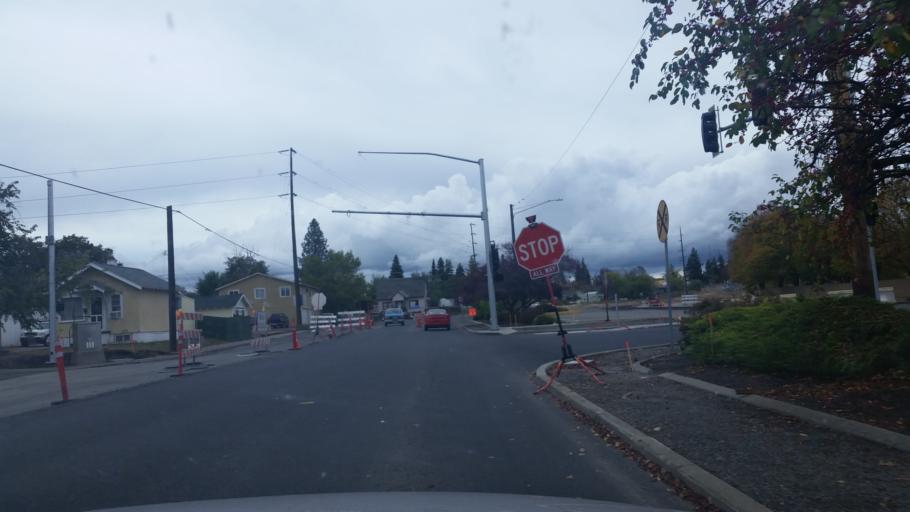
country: US
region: Washington
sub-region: Spokane County
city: Spokane
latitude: 47.6745
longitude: -117.3903
